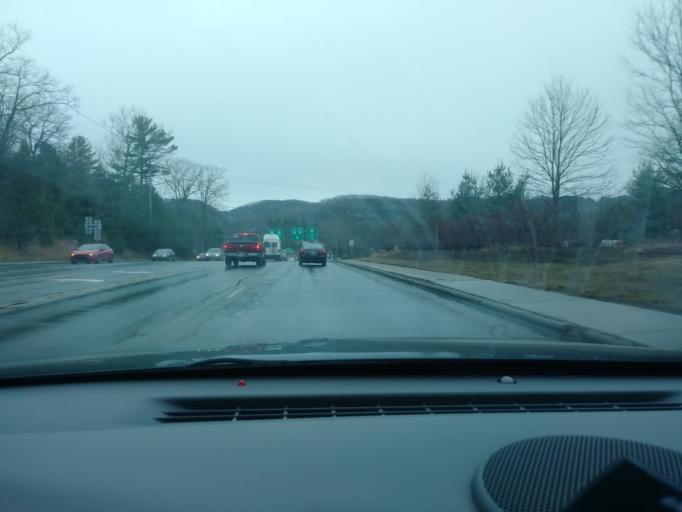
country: US
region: North Carolina
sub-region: Watauga County
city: Boone
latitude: 36.2076
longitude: -81.6676
